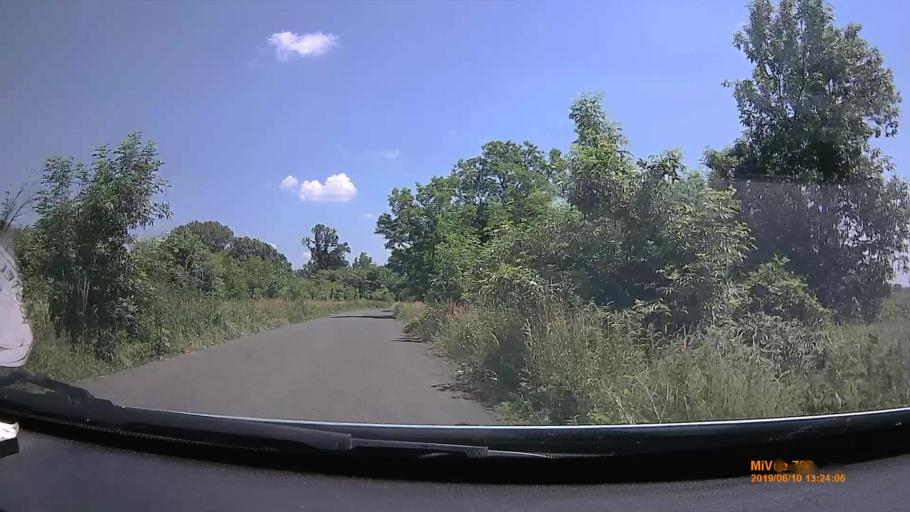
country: HU
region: Borsod-Abauj-Zemplen
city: Tiszaluc
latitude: 48.0230
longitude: 21.0996
